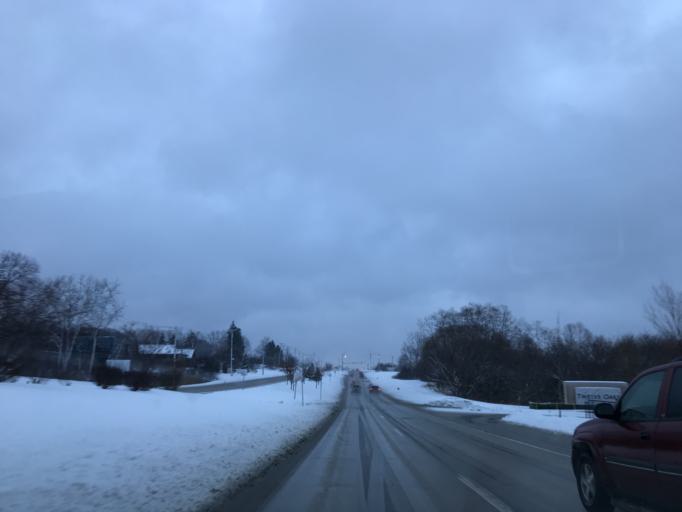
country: US
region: Michigan
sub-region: Oakland County
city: Novi
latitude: 42.4956
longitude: -83.4712
